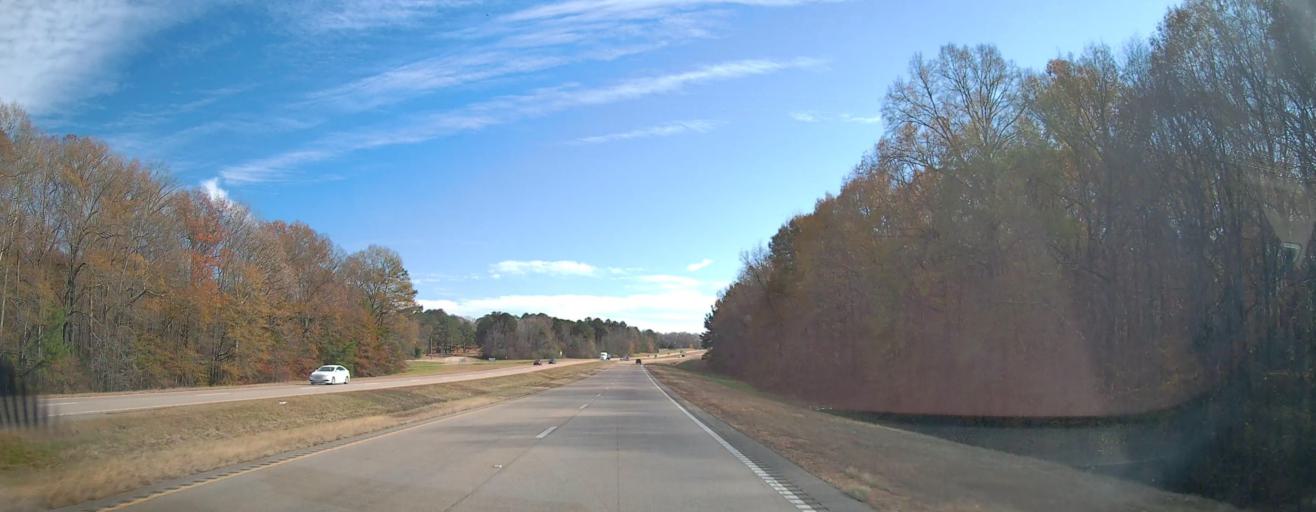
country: US
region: Mississippi
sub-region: Tishomingo County
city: Iuka
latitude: 34.8255
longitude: -88.2992
